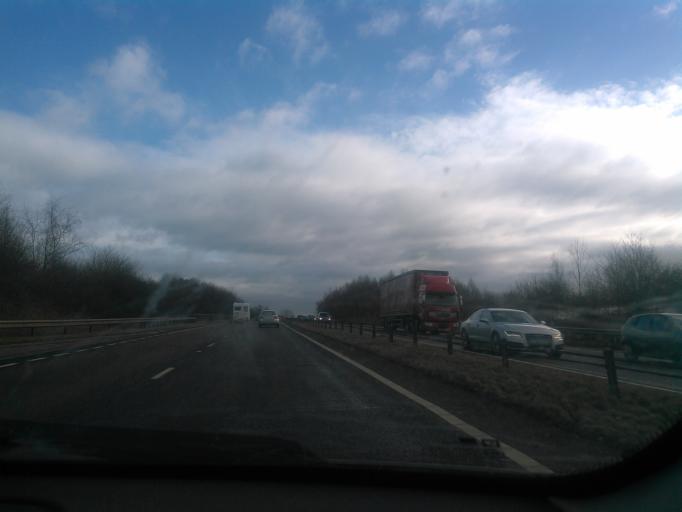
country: GB
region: England
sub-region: Staffordshire
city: Uttoxeter
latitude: 52.8939
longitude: -1.7765
